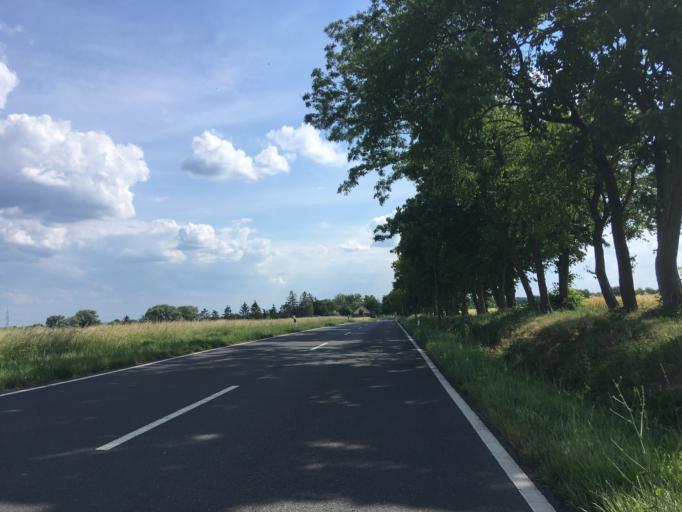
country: DE
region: Brandenburg
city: Muncheberg
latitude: 52.4411
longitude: 14.1014
